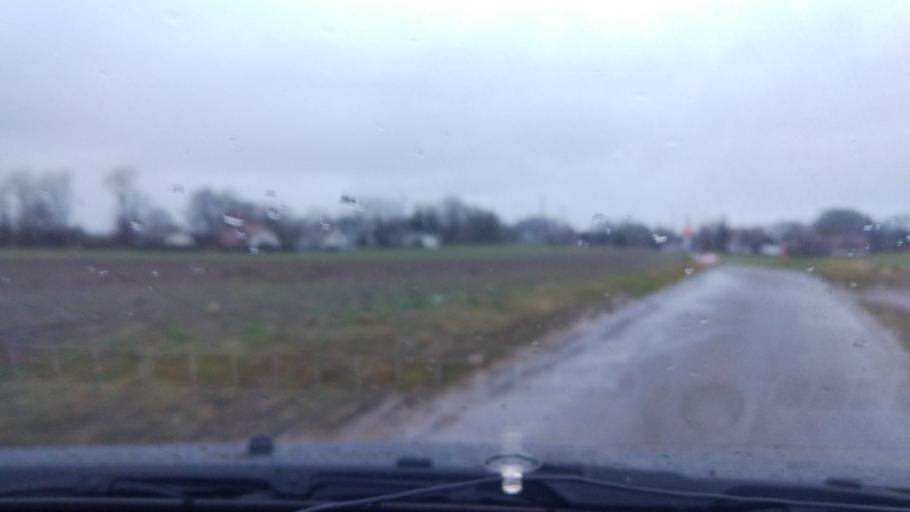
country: CH
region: Vaud
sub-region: Lausanne District
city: Le Mont-sur-Lausanne
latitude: 46.5553
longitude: 6.6257
